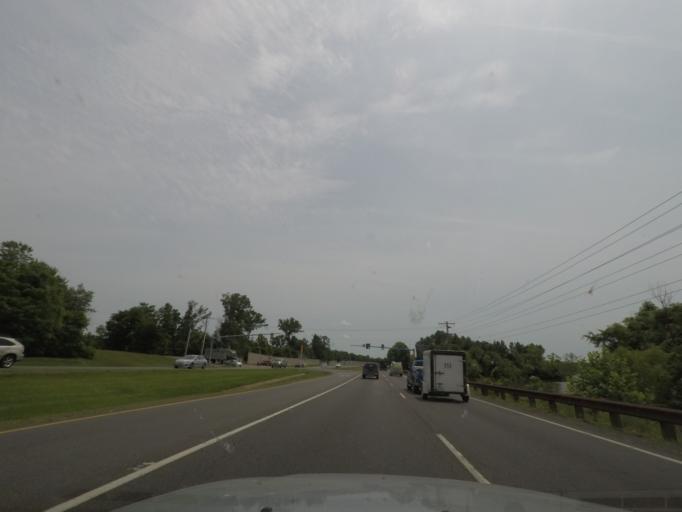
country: US
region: Virginia
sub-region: Prince William County
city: Haymarket
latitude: 38.8369
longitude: -77.6342
